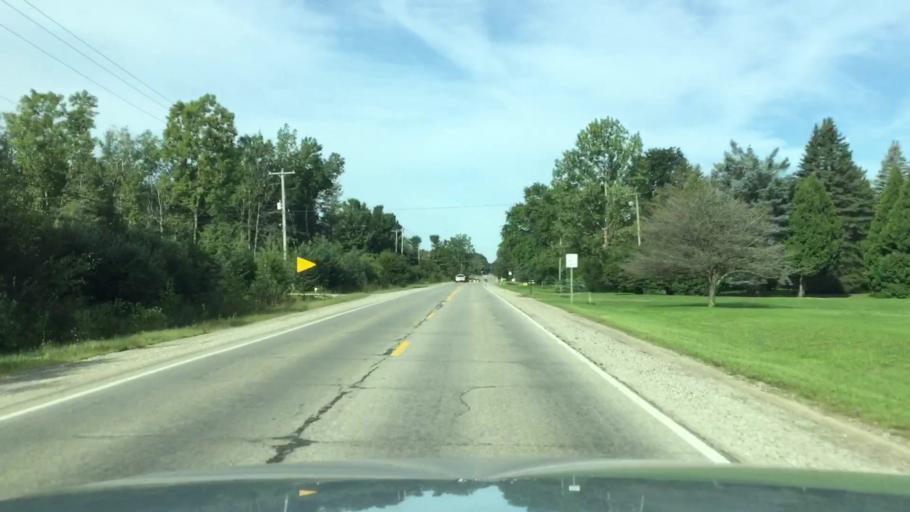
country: US
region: Michigan
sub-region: Genesee County
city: Flushing
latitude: 43.1179
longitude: -83.8216
